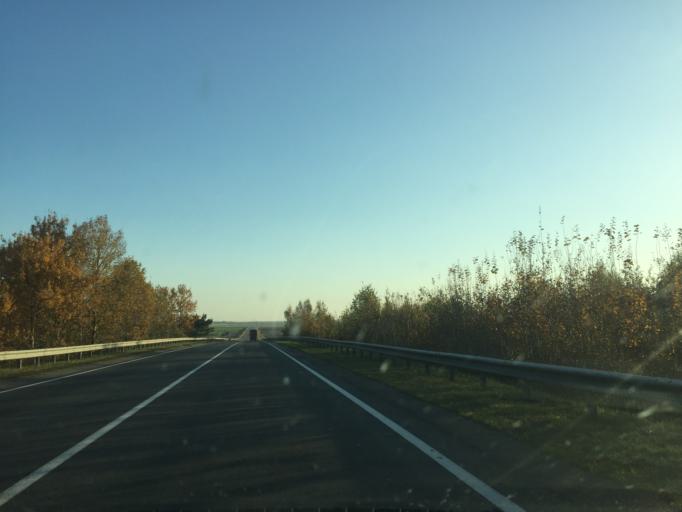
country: BY
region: Mogilev
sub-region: Mahilyowski Rayon
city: Kadino
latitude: 53.8574
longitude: 30.4799
